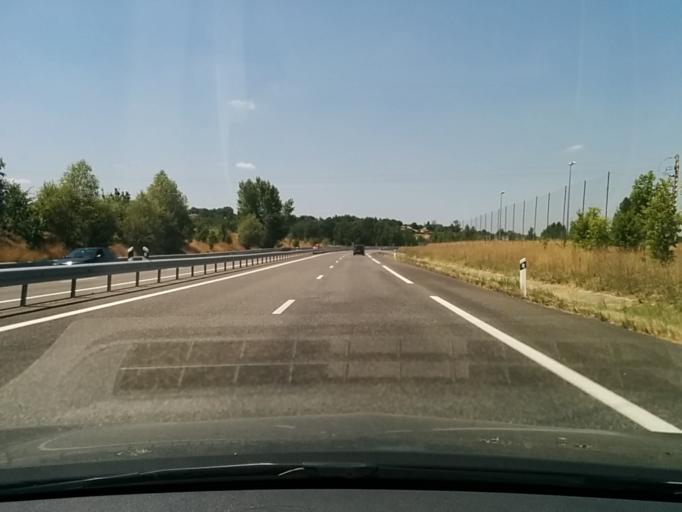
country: FR
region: Midi-Pyrenees
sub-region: Departement du Gers
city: Pujaudran
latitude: 43.6002
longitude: 1.0900
